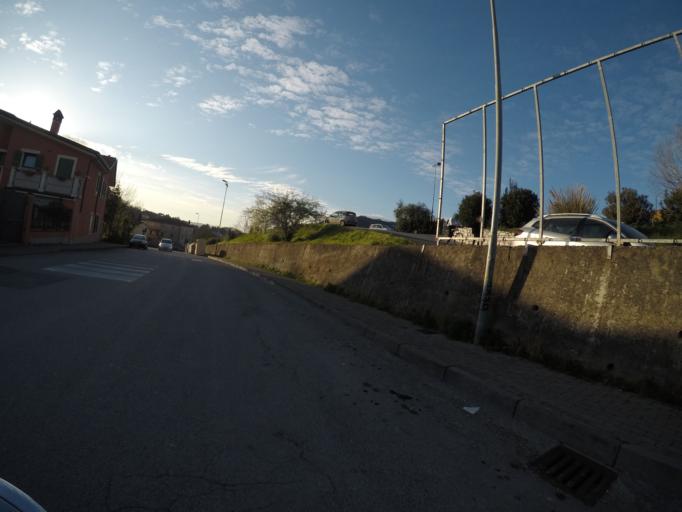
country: IT
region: Tuscany
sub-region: Provincia di Massa-Carrara
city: Carrara
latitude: 44.0575
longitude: 10.0879
